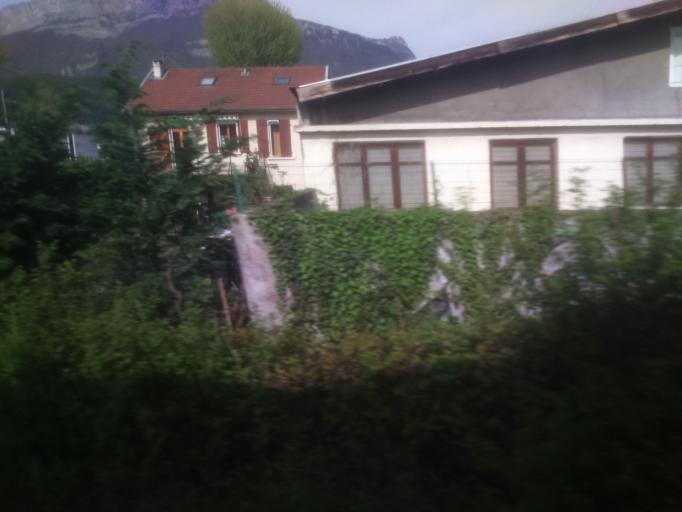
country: FR
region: Rhone-Alpes
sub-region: Departement de l'Isere
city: Grenoble
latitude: 45.1485
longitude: 5.7065
